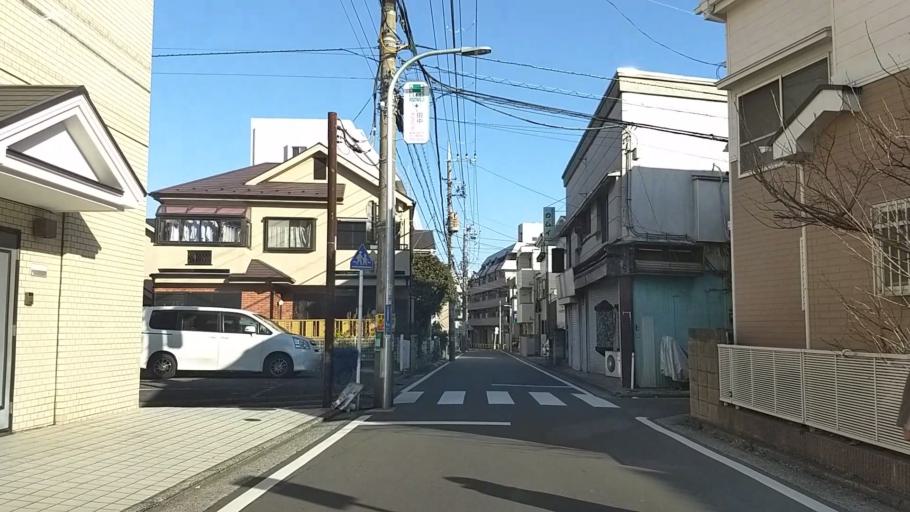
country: JP
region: Kanagawa
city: Yokohama
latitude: 35.4284
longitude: 139.6125
